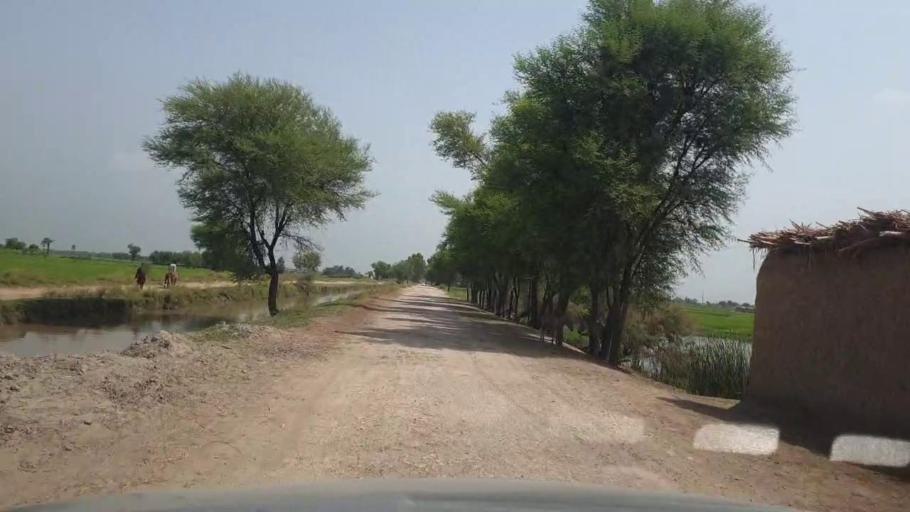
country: PK
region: Sindh
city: Ratodero
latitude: 27.9227
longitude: 68.3562
